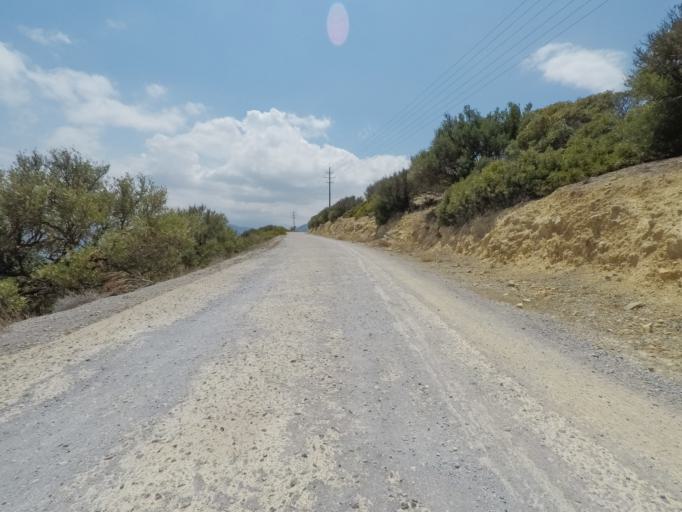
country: GR
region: Crete
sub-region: Nomos Lasithiou
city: Elounda
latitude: 35.3163
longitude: 25.7455
